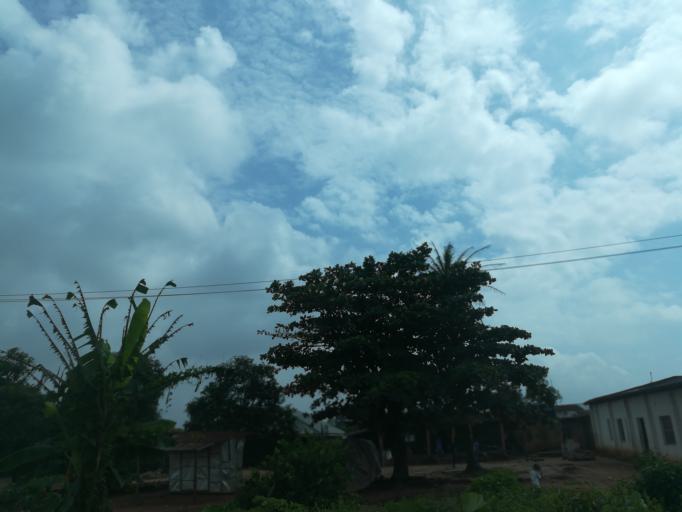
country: NG
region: Lagos
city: Ikorodu
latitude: 6.6696
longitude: 3.6716
